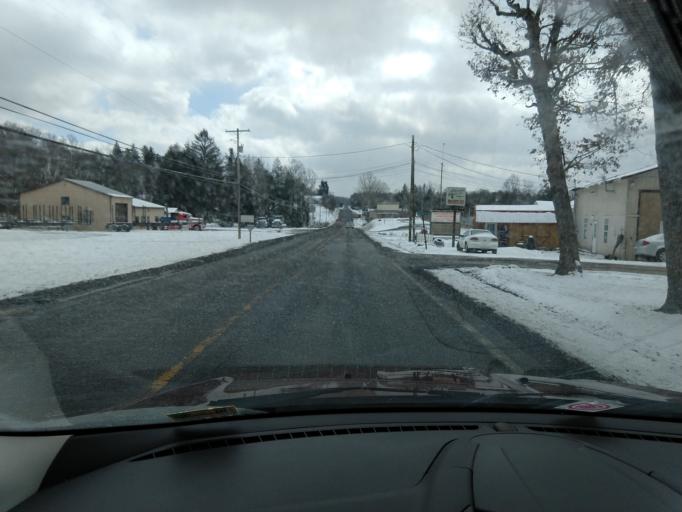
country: US
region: West Virginia
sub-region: Nicholas County
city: Craigsville
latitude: 38.3233
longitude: -80.6538
